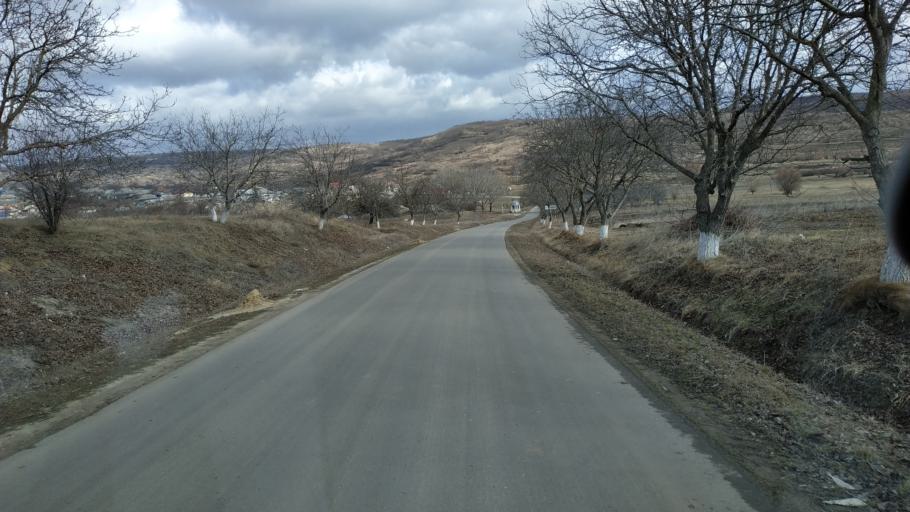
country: MD
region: Stinga Nistrului
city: Bucovat
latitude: 47.2020
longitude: 28.4929
